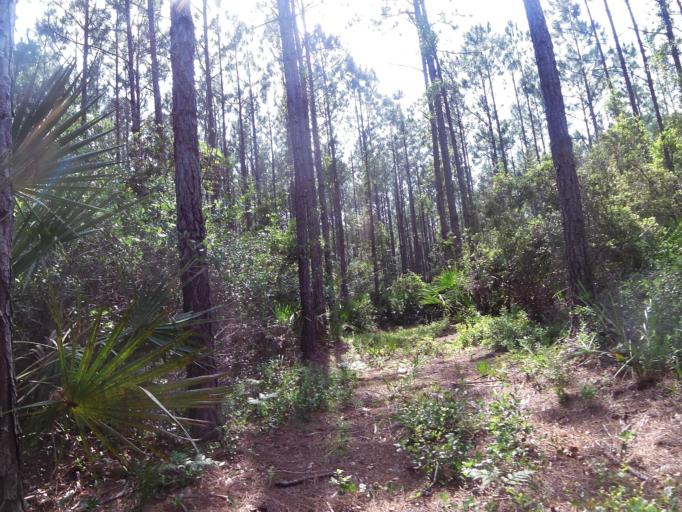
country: US
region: Florida
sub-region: Nassau County
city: Yulee
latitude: 30.4883
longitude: -81.4979
